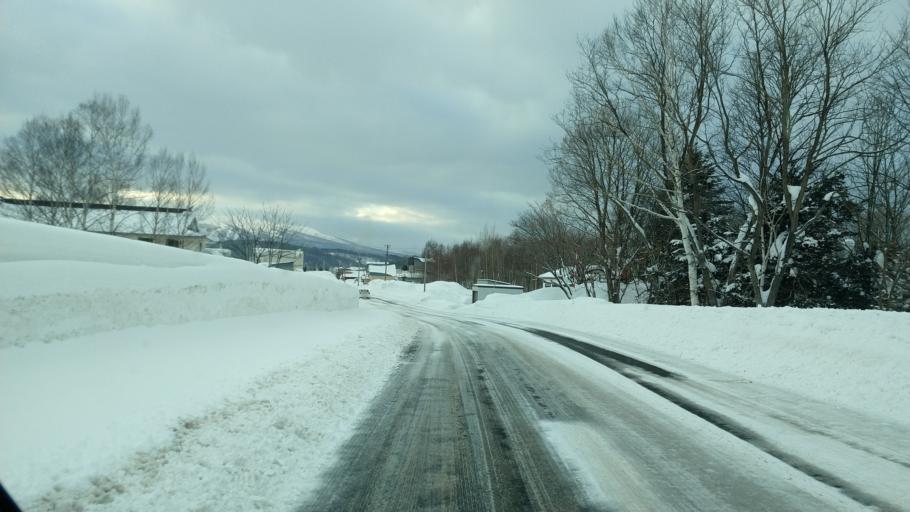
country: JP
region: Hokkaido
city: Niseko Town
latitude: 42.9079
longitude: 140.7735
